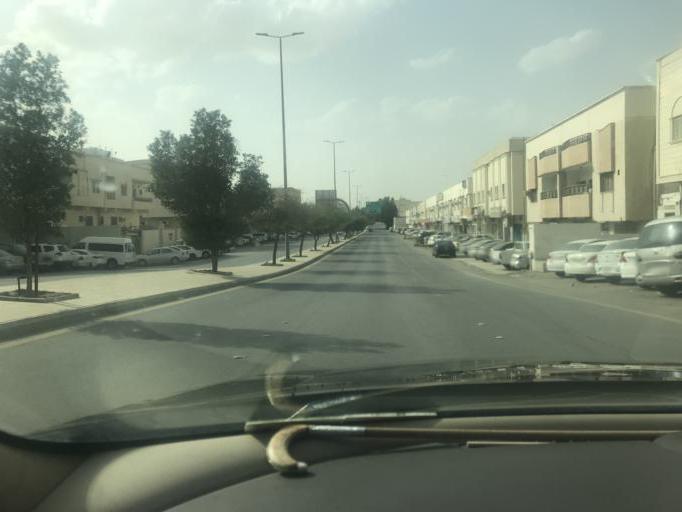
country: SA
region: Ar Riyad
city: Riyadh
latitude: 24.7280
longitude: 46.7645
